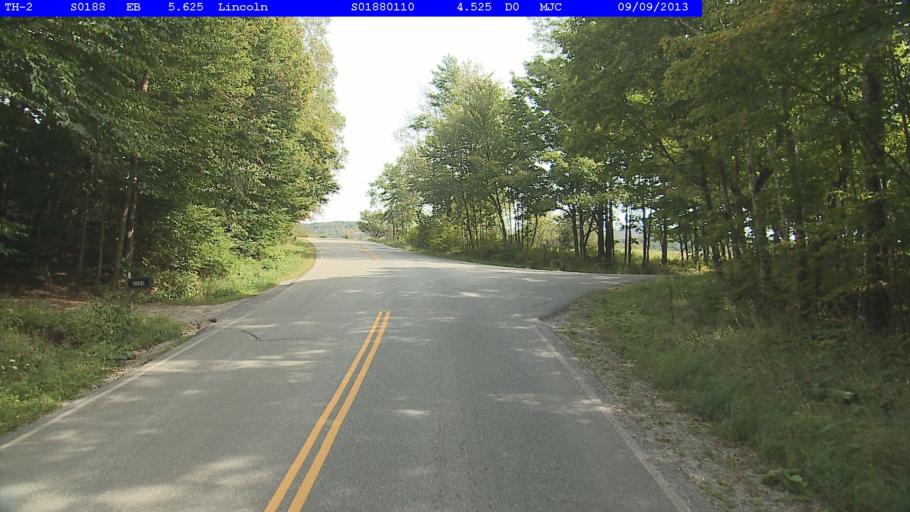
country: US
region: Vermont
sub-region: Addison County
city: Bristol
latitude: 44.0946
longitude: -72.9623
